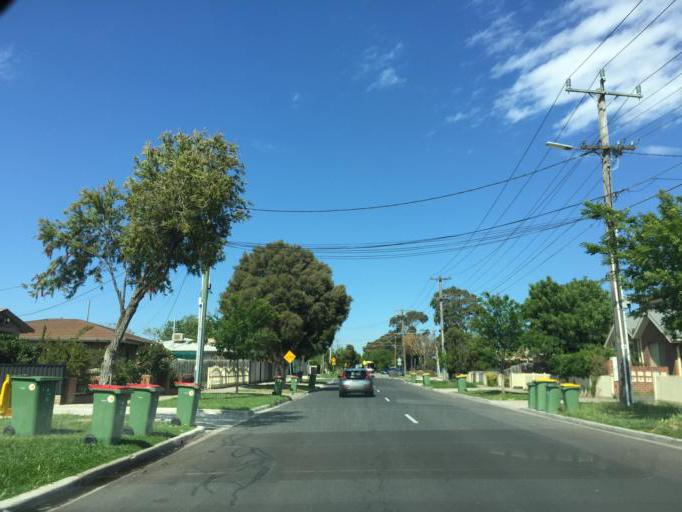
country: AU
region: Victoria
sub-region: Maribyrnong
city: Braybrook
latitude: -37.7828
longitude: 144.8514
